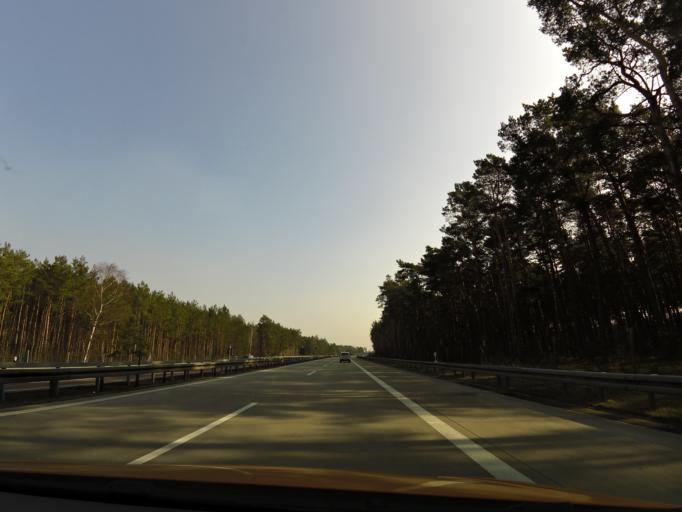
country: DE
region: Brandenburg
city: Briesen
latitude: 52.3359
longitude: 14.2406
